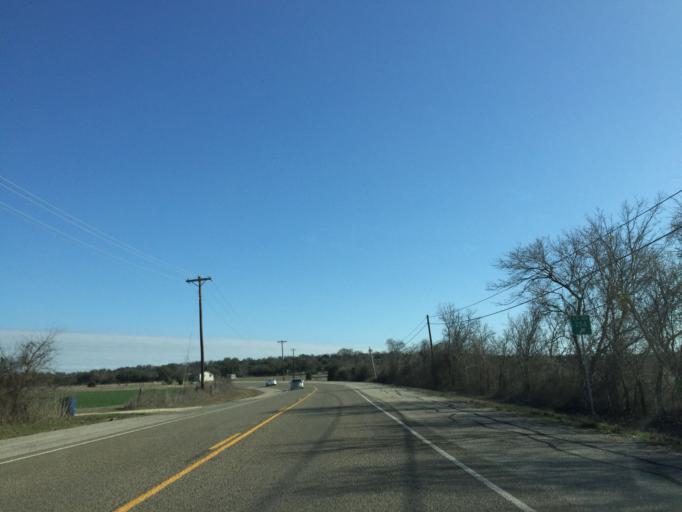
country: US
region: Texas
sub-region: Williamson County
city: Florence
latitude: 30.7676
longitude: -97.8463
